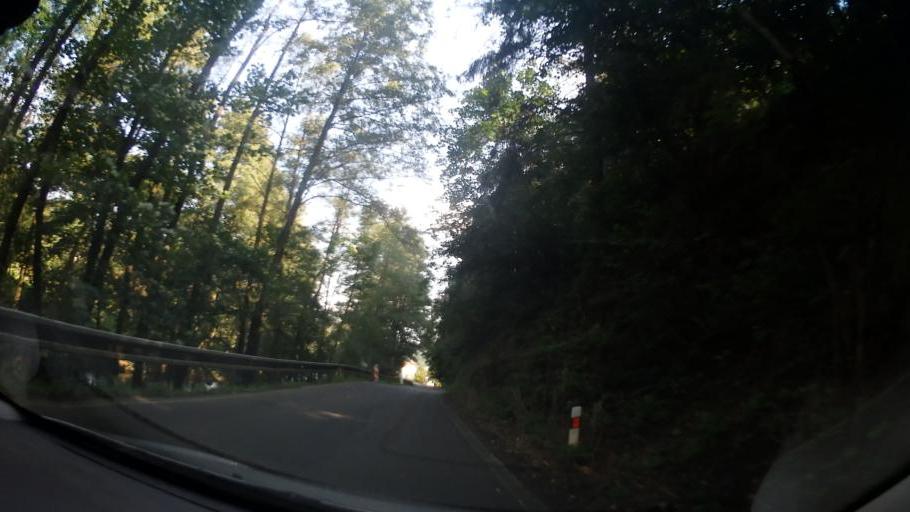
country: CZ
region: South Moravian
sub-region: Okres Brno-Venkov
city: Nedvedice
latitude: 49.5252
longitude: 16.3450
